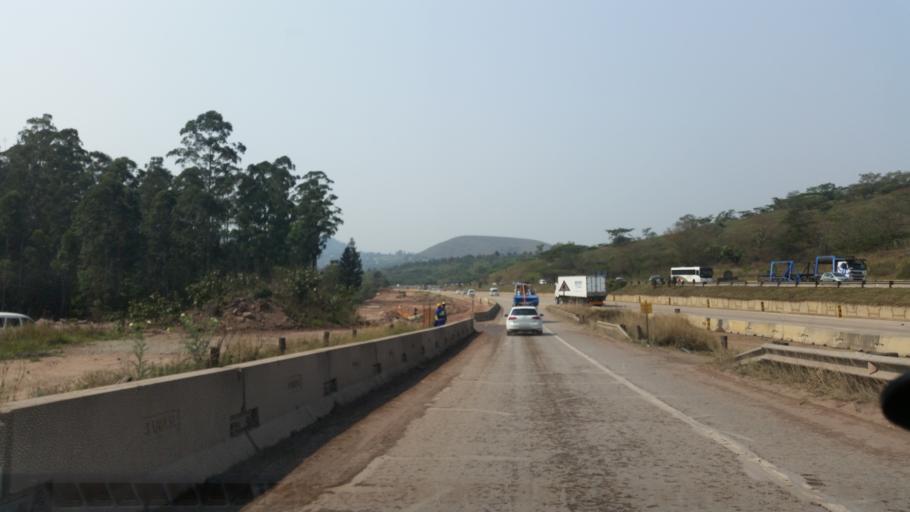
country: ZA
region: KwaZulu-Natal
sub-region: eThekwini Metropolitan Municipality
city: Mpumalanga
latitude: -29.7581
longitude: 30.6676
